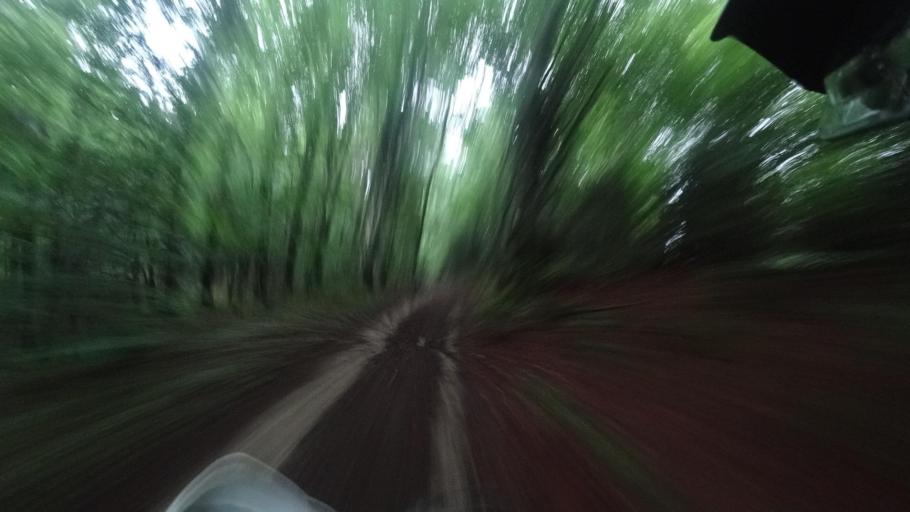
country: HR
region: Licko-Senjska
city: Jezerce
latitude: 44.8199
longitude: 15.6181
